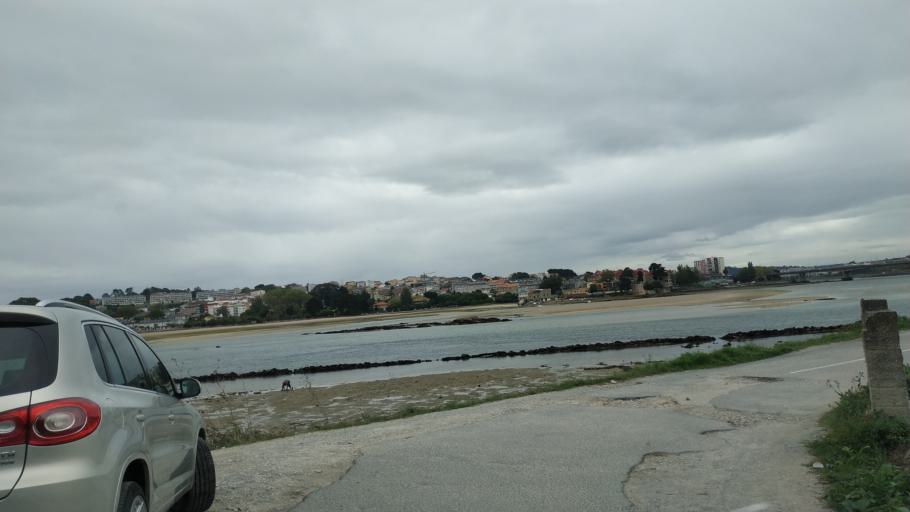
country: ES
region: Galicia
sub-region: Provincia da Coruna
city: A Coruna
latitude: 43.3386
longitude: -8.3865
